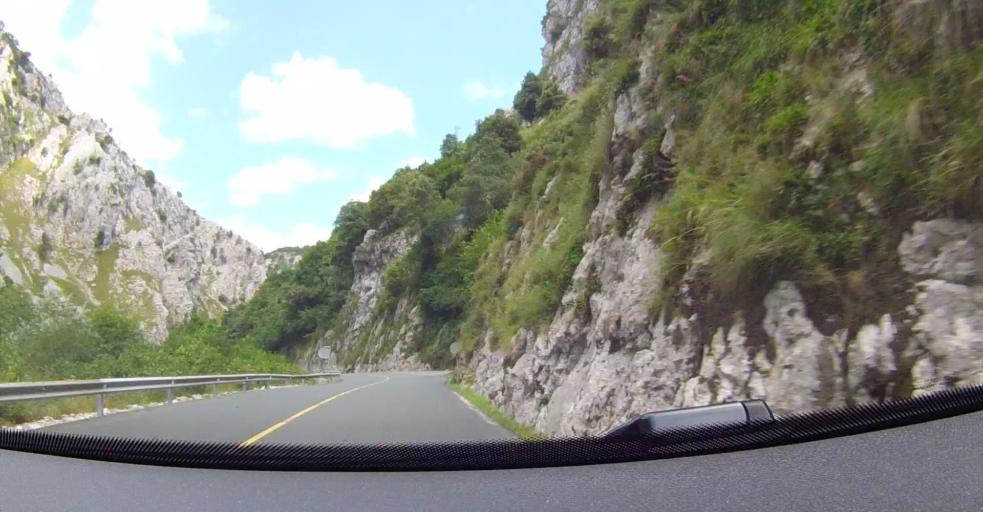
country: ES
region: Cantabria
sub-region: Provincia de Cantabria
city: Tresviso
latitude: 43.2998
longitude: -4.6065
